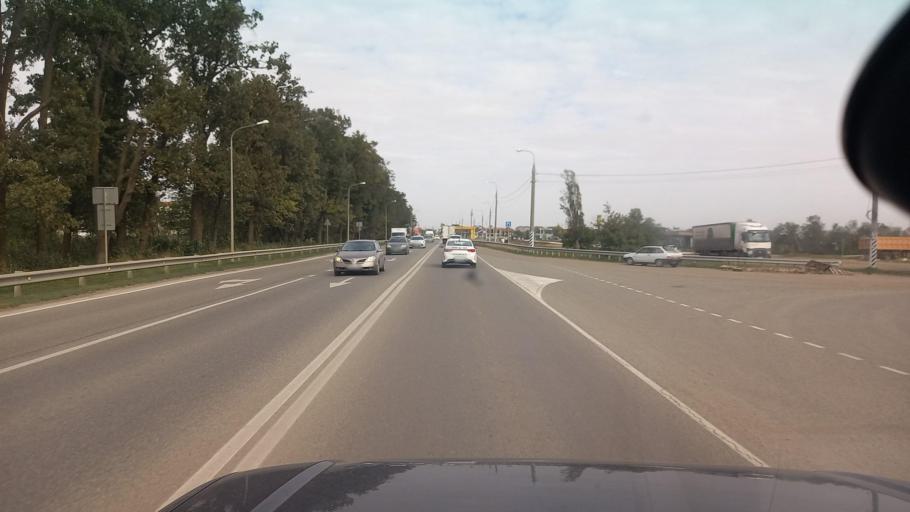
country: RU
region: Krasnodarskiy
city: Krasnodar
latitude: 45.0989
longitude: 38.9130
